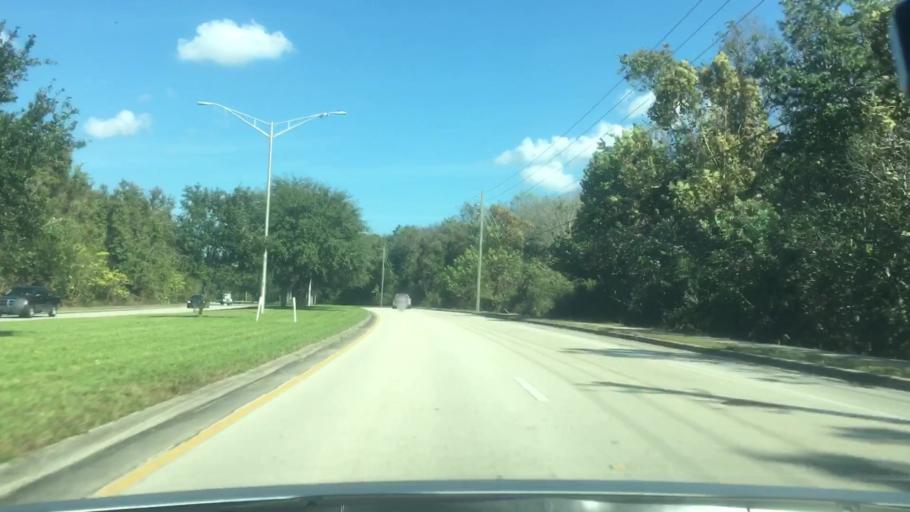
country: US
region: Florida
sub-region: Duval County
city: Atlantic Beach
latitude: 30.3542
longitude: -81.5067
